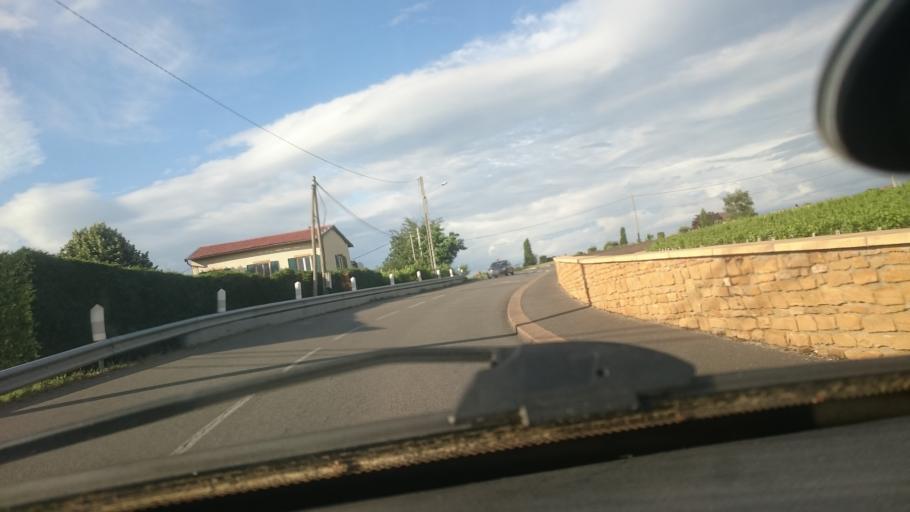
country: FR
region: Rhone-Alpes
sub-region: Departement du Rhone
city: Bully
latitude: 45.8810
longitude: 4.5606
